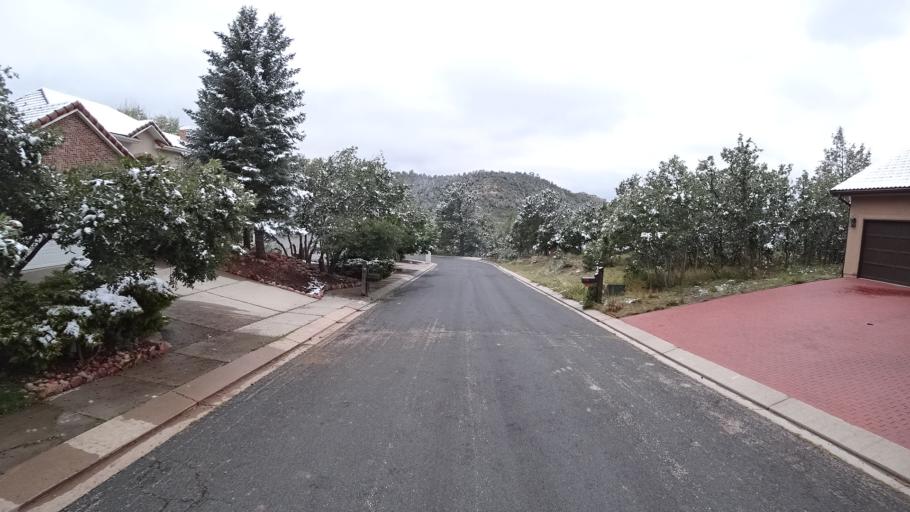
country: US
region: Colorado
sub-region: El Paso County
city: Colorado Springs
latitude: 38.9177
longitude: -104.8025
